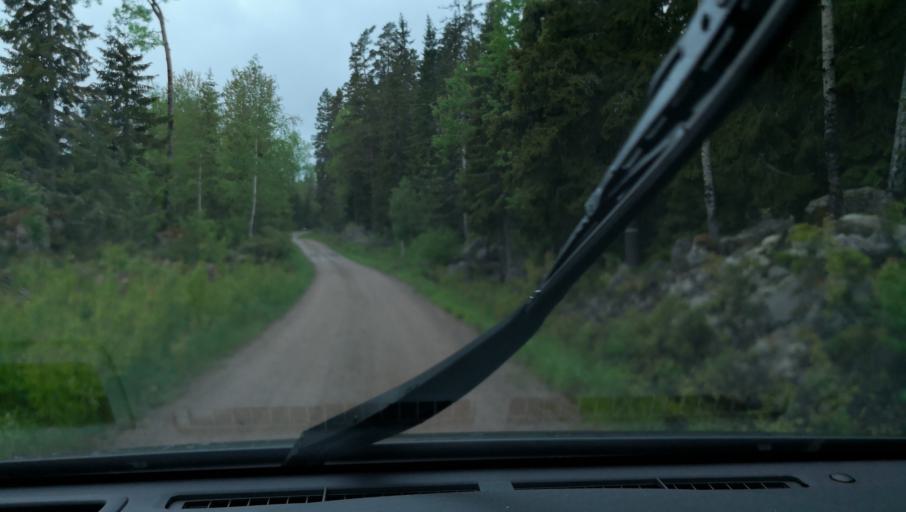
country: SE
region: Uppsala
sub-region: Enkopings Kommun
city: Orsundsbro
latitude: 59.9358
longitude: 17.3177
